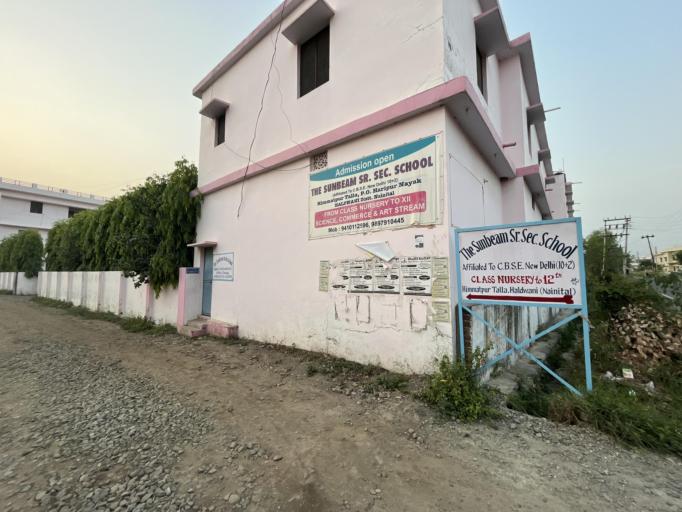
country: IN
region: Uttarakhand
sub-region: Naini Tal
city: Haldwani
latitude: 29.2145
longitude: 79.4766
